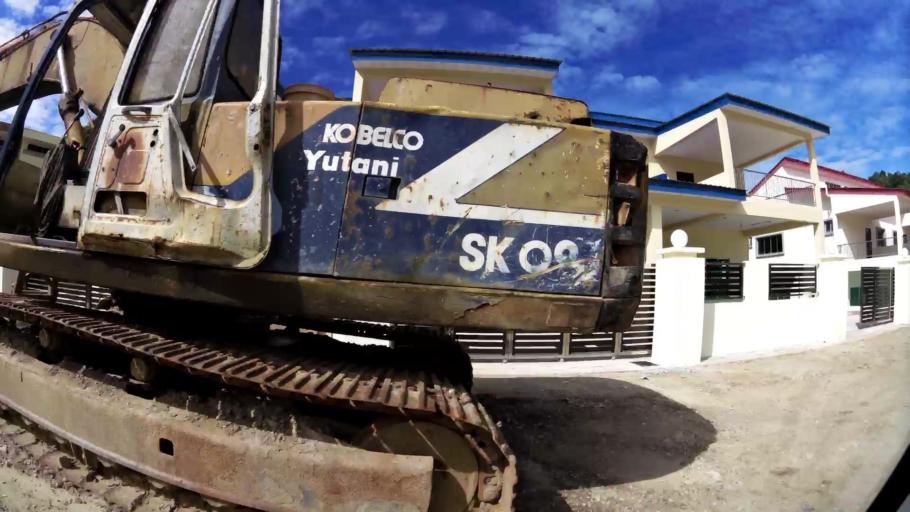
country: BN
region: Brunei and Muara
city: Bandar Seri Begawan
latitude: 4.9059
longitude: 114.9771
